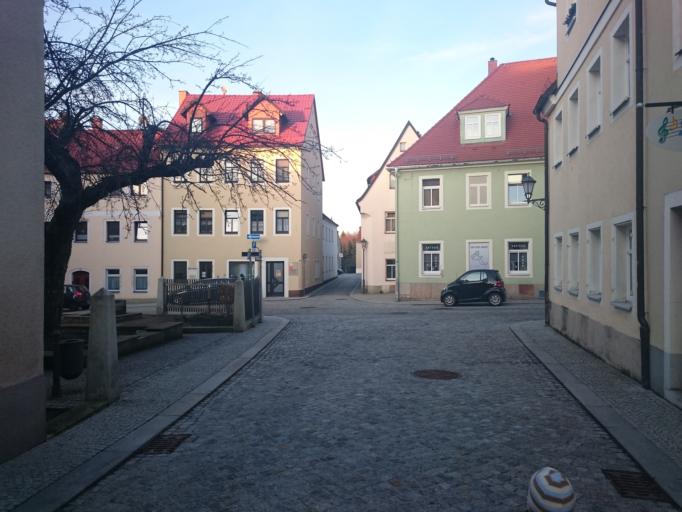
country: DE
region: Saxony
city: Dippoldiswalde
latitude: 50.8963
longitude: 13.6692
